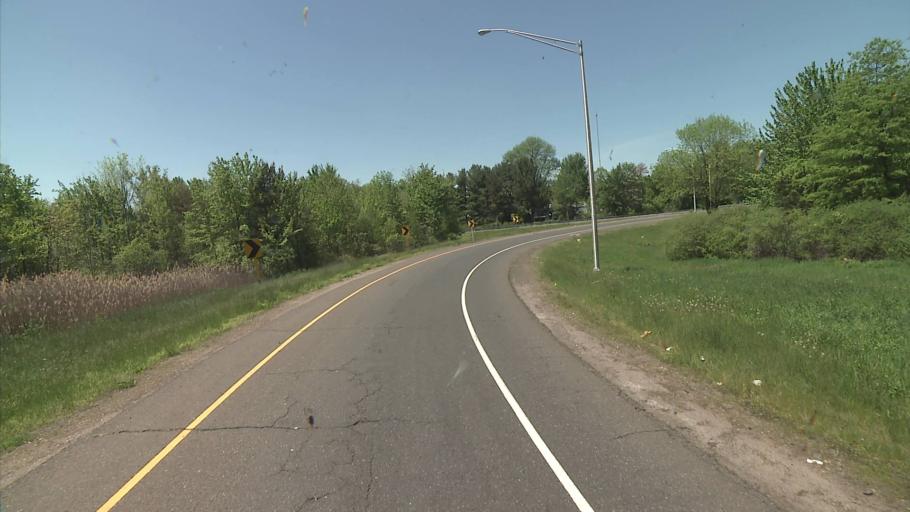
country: US
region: Connecticut
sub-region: Hartford County
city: Farmington
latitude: 41.7050
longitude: -72.8040
